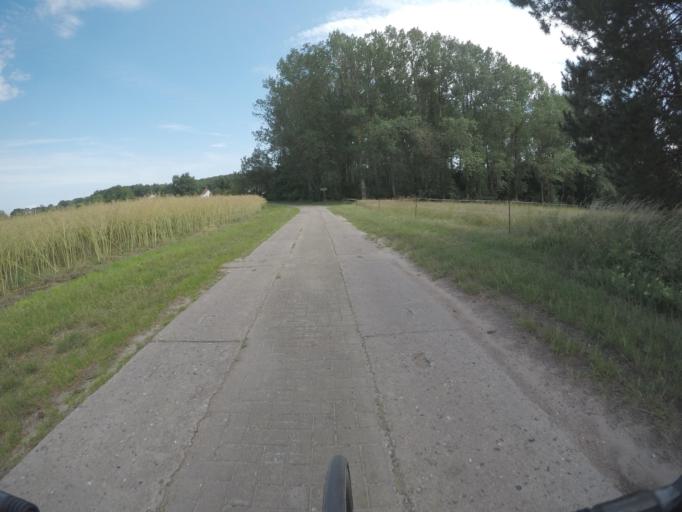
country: DE
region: Mecklenburg-Vorpommern
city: Rambin
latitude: 54.3641
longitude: 13.1636
